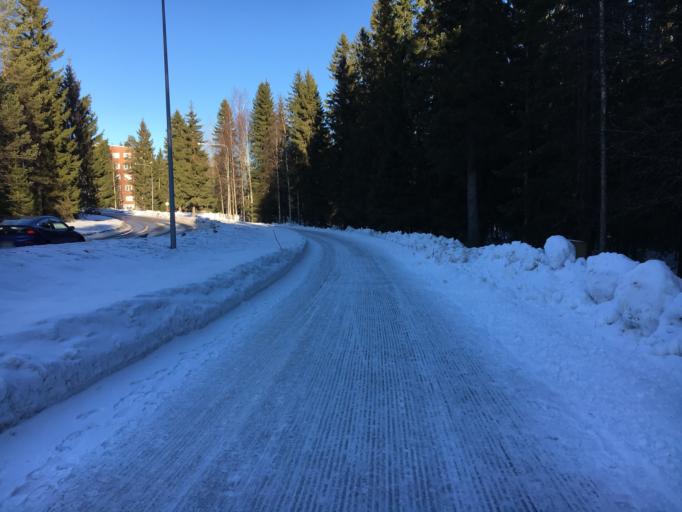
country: FI
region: Kainuu
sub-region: Kajaani
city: Kajaani
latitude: 64.2274
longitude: 27.7491
